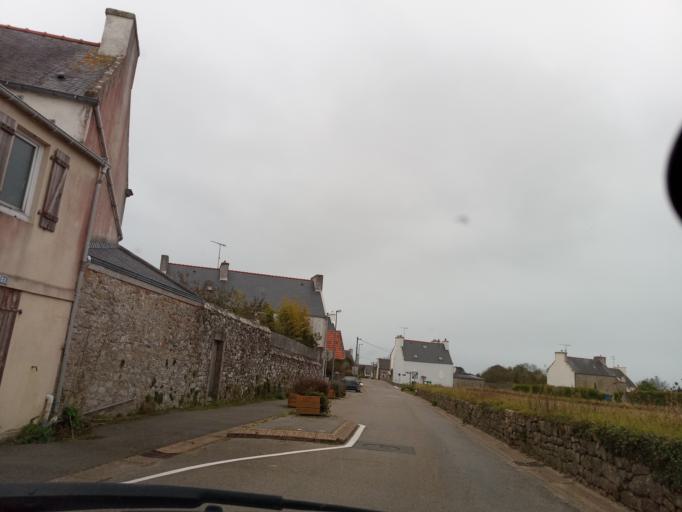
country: FR
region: Brittany
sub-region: Departement du Finistere
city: Esquibien
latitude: 48.0228
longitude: -4.5633
